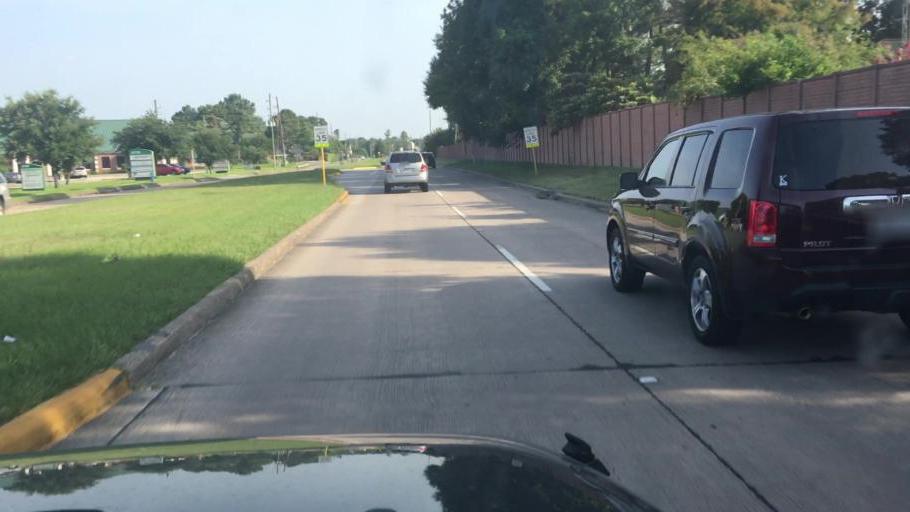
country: US
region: Texas
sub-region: Harris County
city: Atascocita
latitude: 29.9909
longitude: -95.1618
